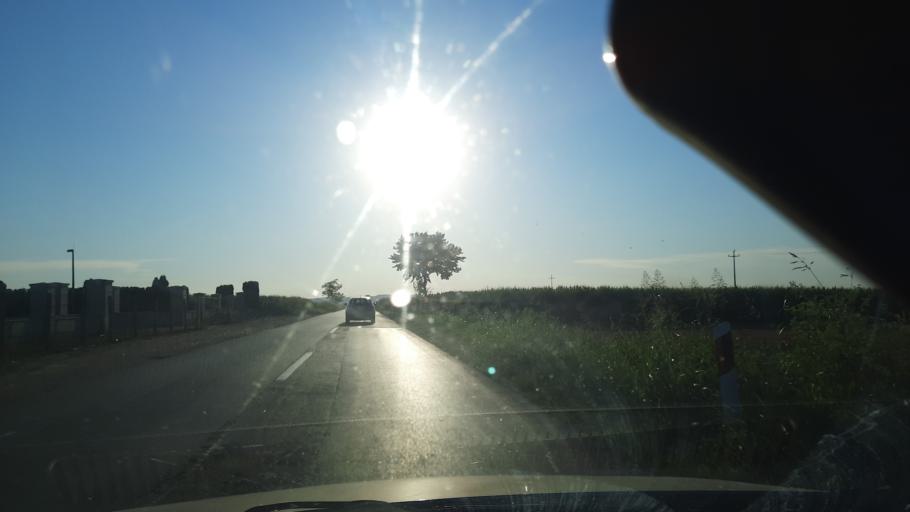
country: RS
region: Central Serbia
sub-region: Branicevski Okrug
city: Malo Crnice
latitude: 44.5834
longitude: 21.3020
